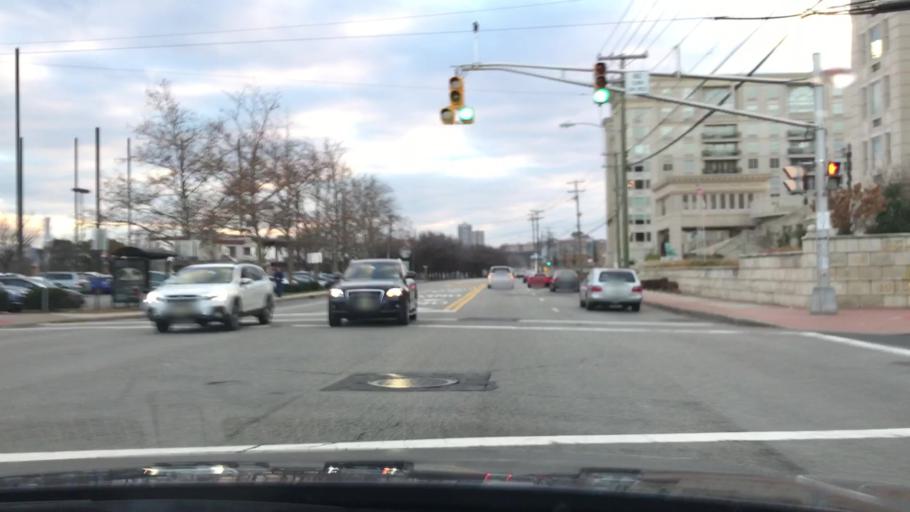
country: US
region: New Jersey
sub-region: Bergen County
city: Cliffside Park
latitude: 40.8170
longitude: -73.9808
